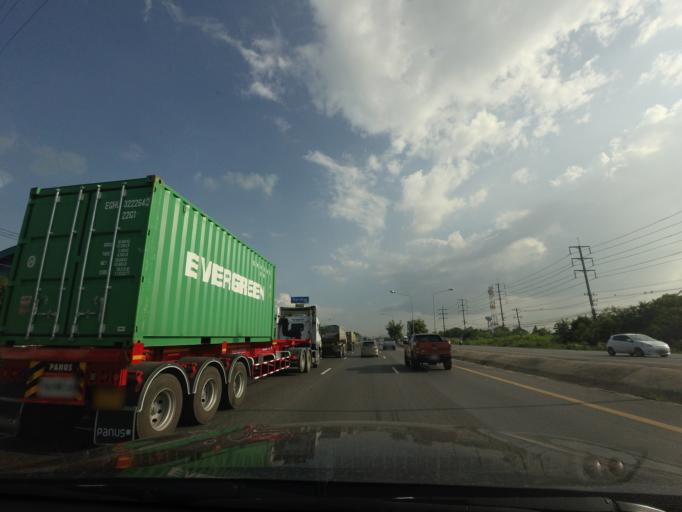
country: TH
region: Sara Buri
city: Chaloem Phra Kiat
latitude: 14.5788
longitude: 100.9011
